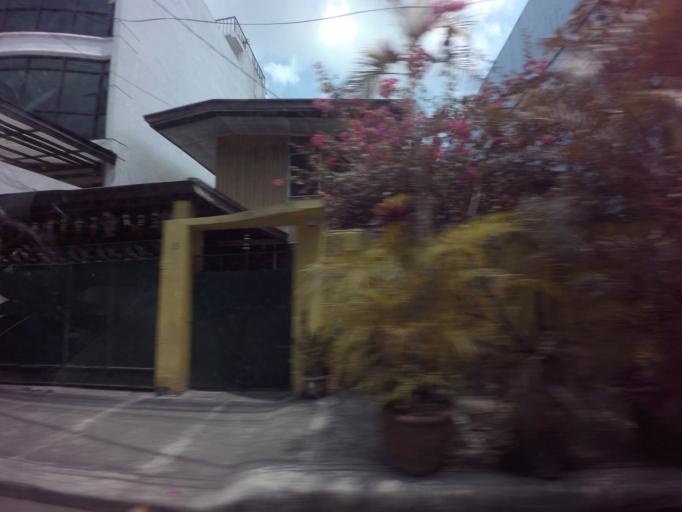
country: PH
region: Metro Manila
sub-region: Makati City
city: Makati City
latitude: 14.5627
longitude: 121.0334
